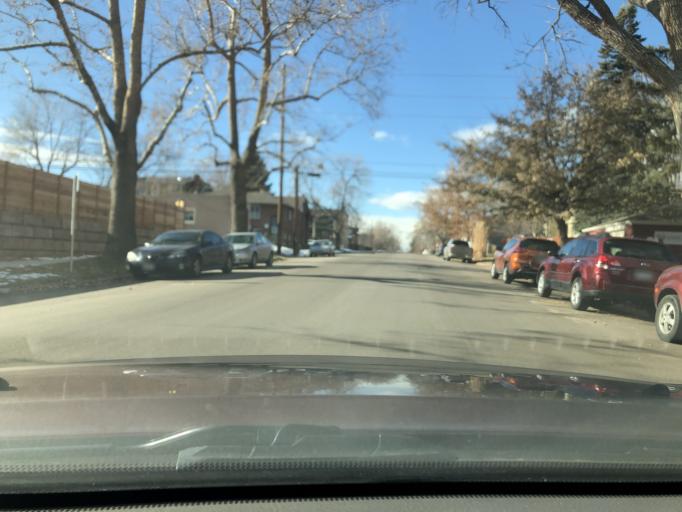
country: US
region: Colorado
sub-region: Denver County
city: Denver
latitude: 39.7533
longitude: -104.9611
